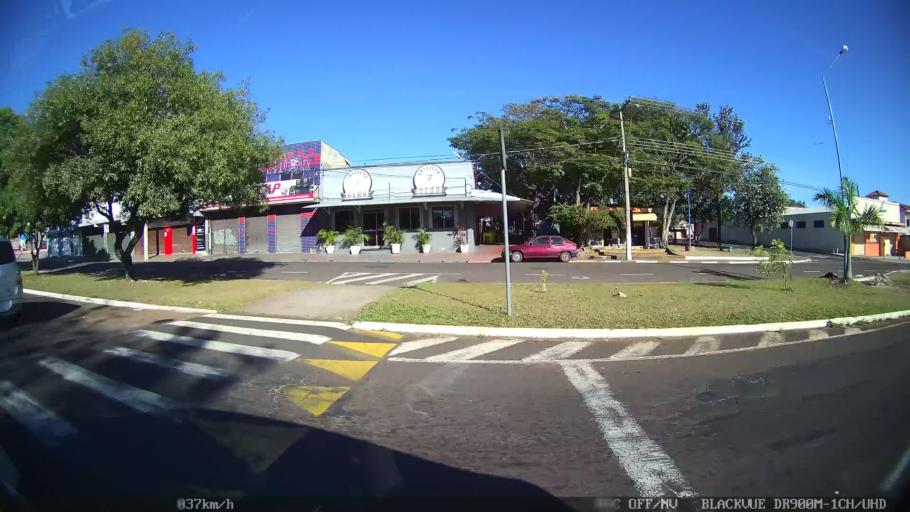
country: BR
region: Sao Paulo
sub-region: Franca
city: Franca
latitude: -20.5607
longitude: -47.3956
